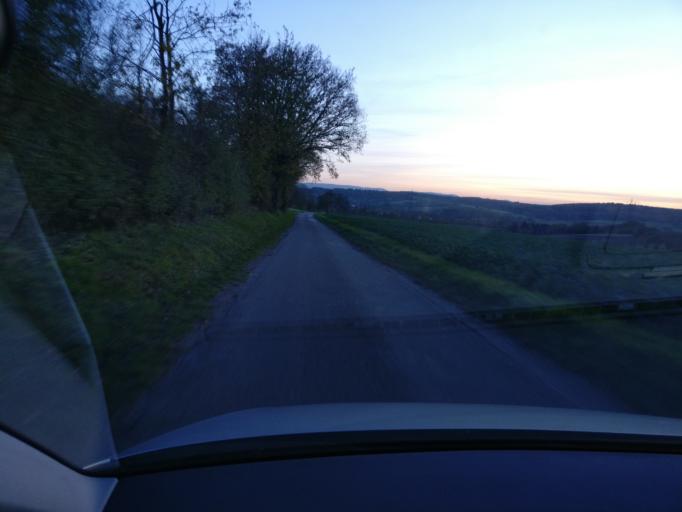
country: DE
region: Baden-Wuerttemberg
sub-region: Karlsruhe Region
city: Woessingen
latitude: 49.0252
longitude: 8.6082
